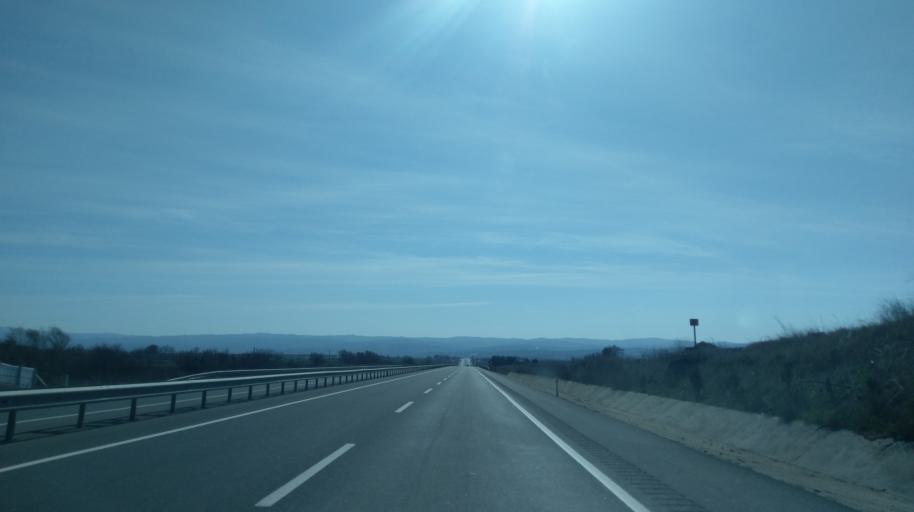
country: TR
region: Edirne
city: Kesan
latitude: 40.8003
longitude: 26.6668
